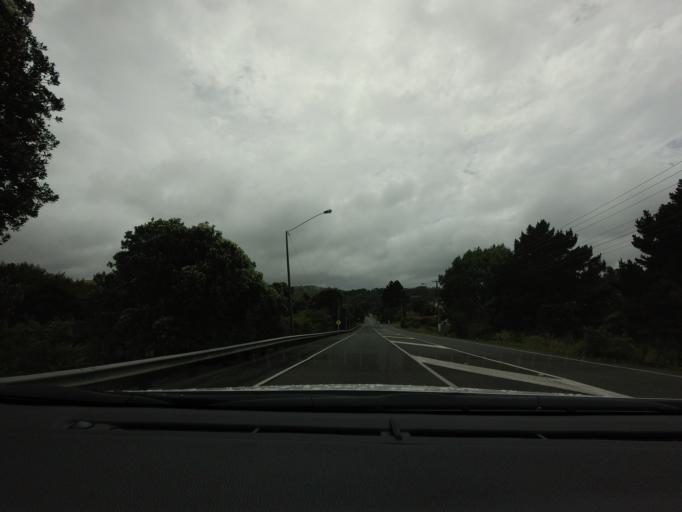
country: NZ
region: Auckland
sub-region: Auckland
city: Rothesay Bay
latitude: -36.5676
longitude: 174.6922
